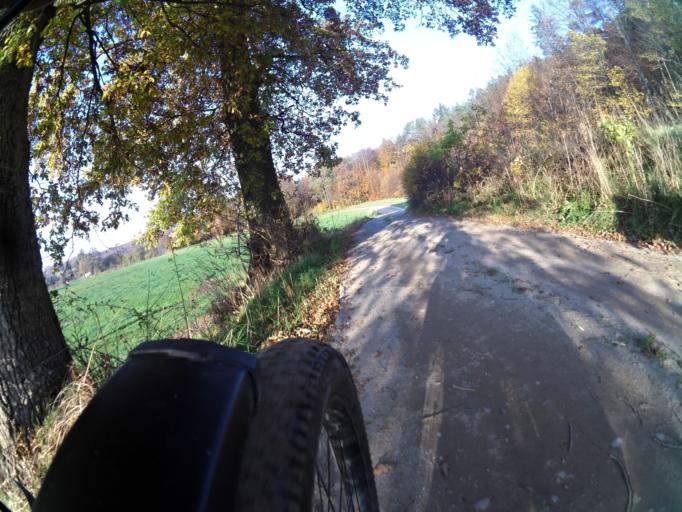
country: PL
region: Pomeranian Voivodeship
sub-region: Powiat pucki
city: Krokowa
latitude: 54.7484
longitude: 18.1956
